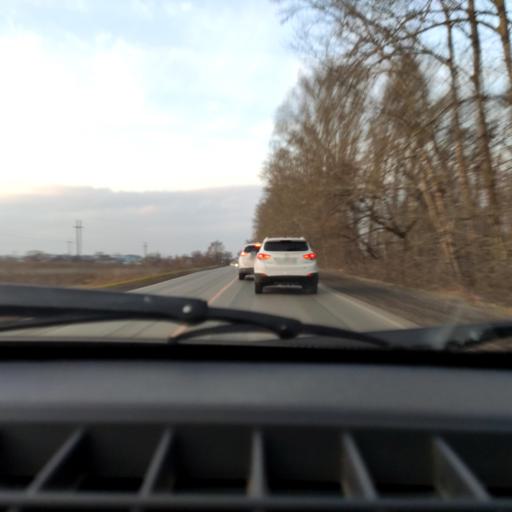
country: RU
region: Bashkortostan
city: Avdon
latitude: 54.7298
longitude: 55.8052
